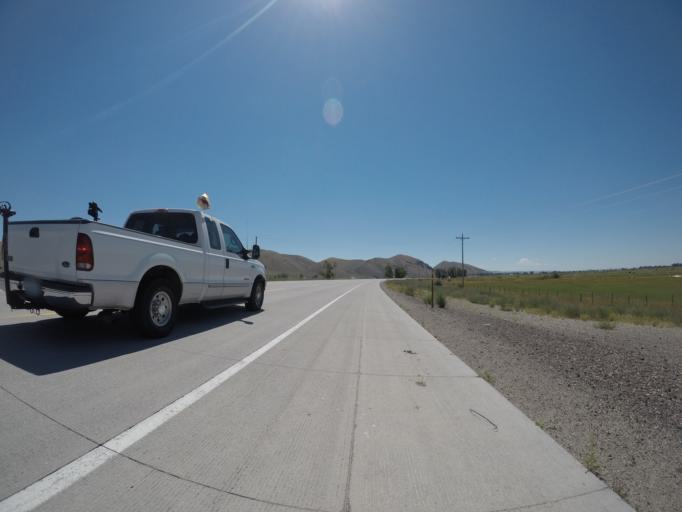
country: US
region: Idaho
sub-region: Bear Lake County
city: Montpelier
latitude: 42.1181
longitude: -110.9611
